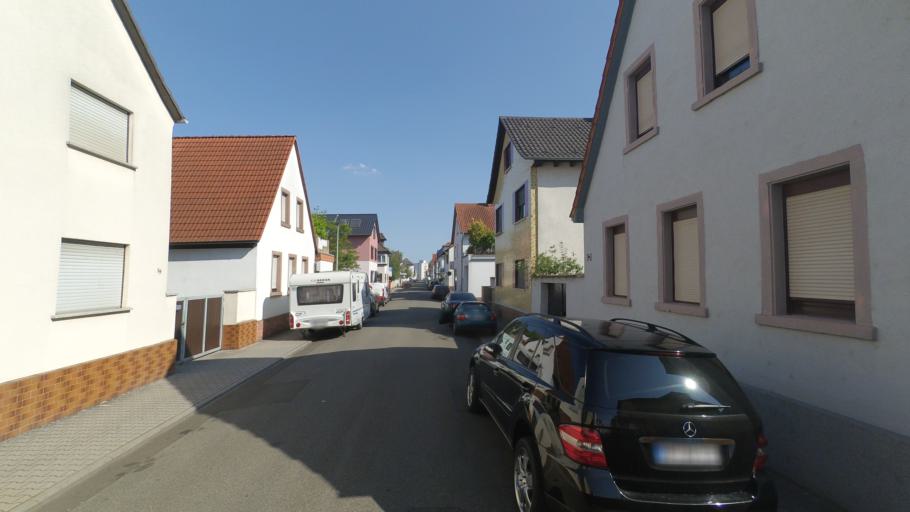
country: DE
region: Hesse
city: Lampertheim
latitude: 49.5983
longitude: 8.4688
